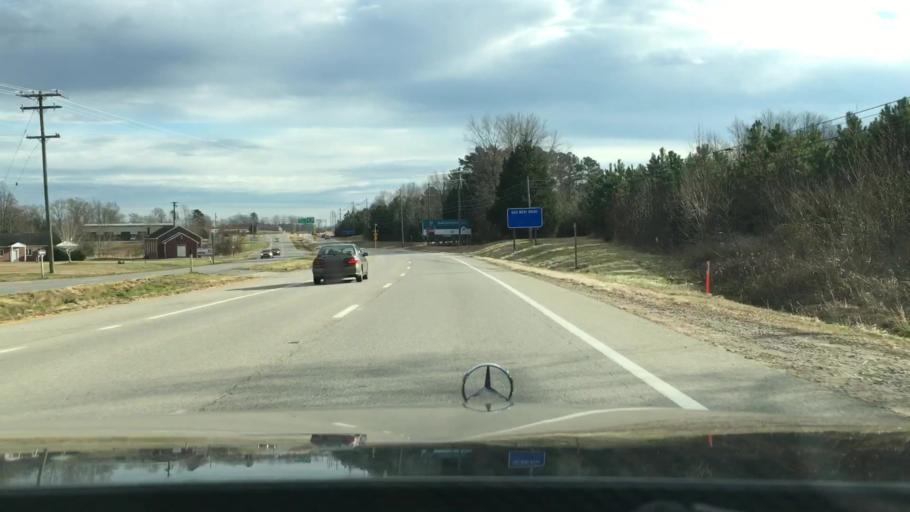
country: US
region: Virginia
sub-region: Pittsylvania County
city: Mount Hermon
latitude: 36.7085
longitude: -79.3743
